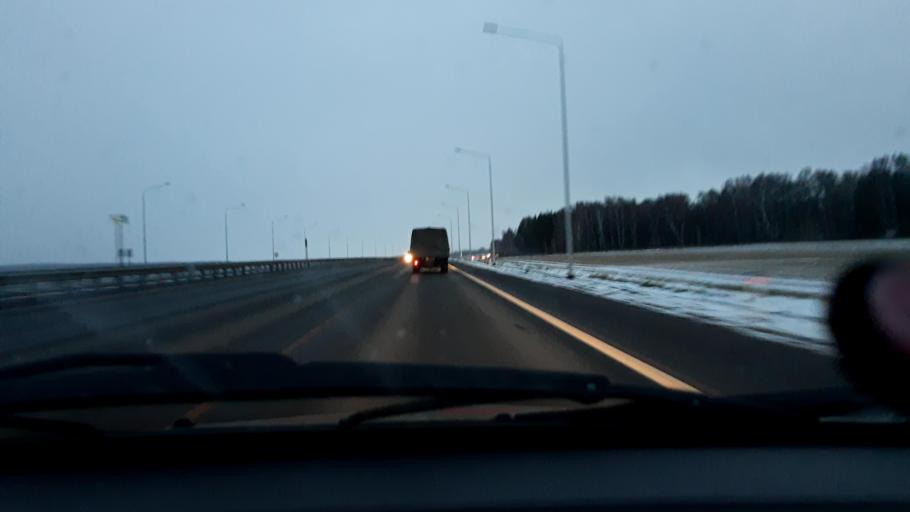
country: RU
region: Bashkortostan
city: Tolbazy
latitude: 54.1439
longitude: 55.9027
